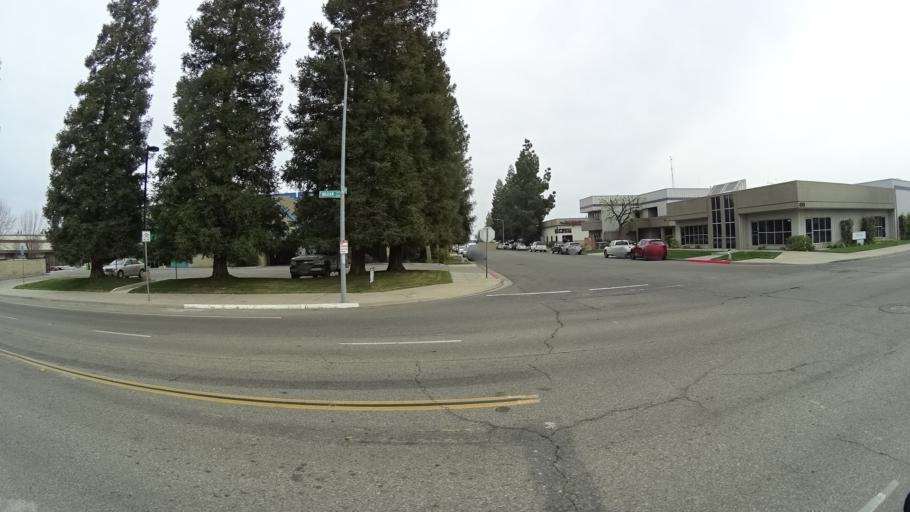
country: US
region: California
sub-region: Fresno County
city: Clovis
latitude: 36.8462
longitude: -119.8019
